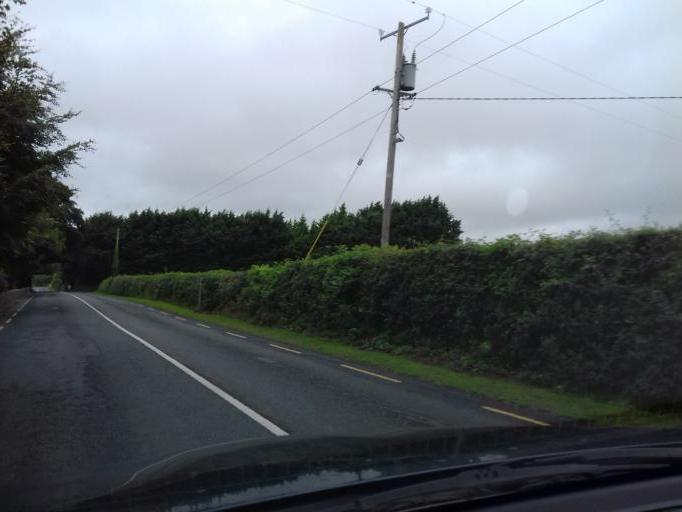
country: IE
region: Leinster
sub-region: County Carlow
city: Bagenalstown
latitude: 52.7139
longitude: -6.9581
